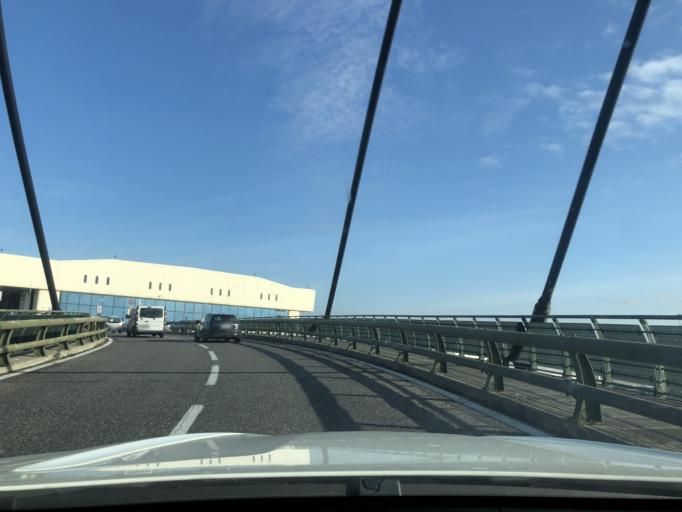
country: IT
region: Lombardy
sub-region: Provincia di Varese
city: Vizzola Ticino
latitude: 45.6242
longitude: 8.7113
